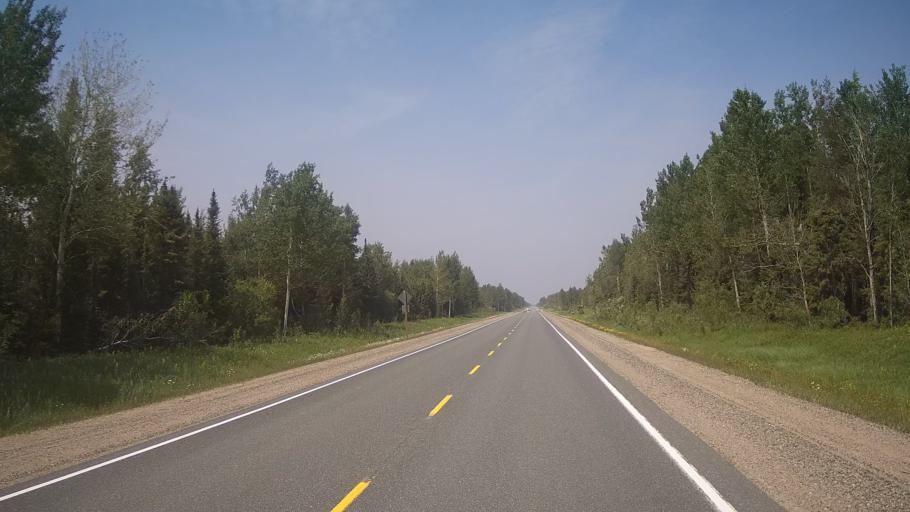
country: CA
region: Ontario
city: Timmins
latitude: 48.8119
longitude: -81.3692
